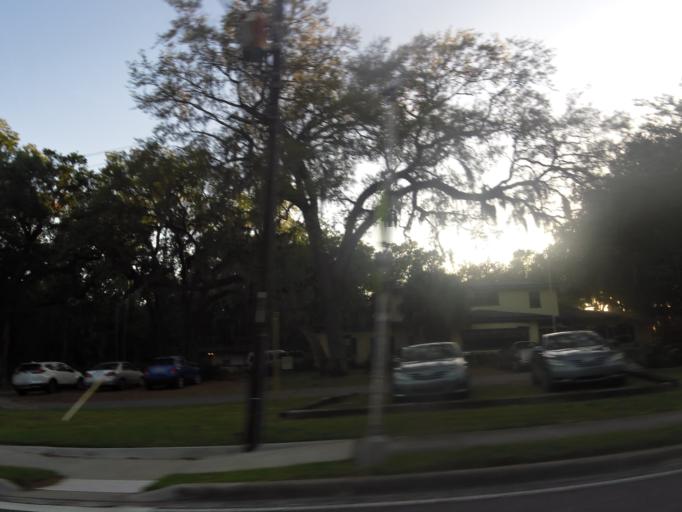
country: US
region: Florida
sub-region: Duval County
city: Jacksonville
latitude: 30.3254
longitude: -81.5849
